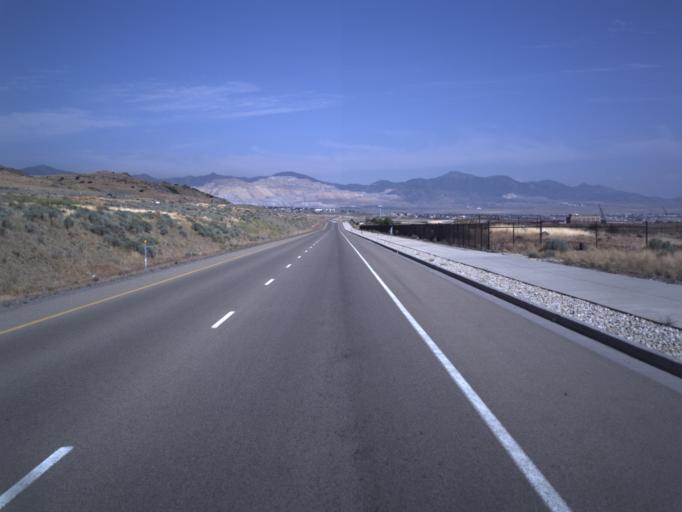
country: US
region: Utah
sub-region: Salt Lake County
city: Bluffdale
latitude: 40.4658
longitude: -111.9572
